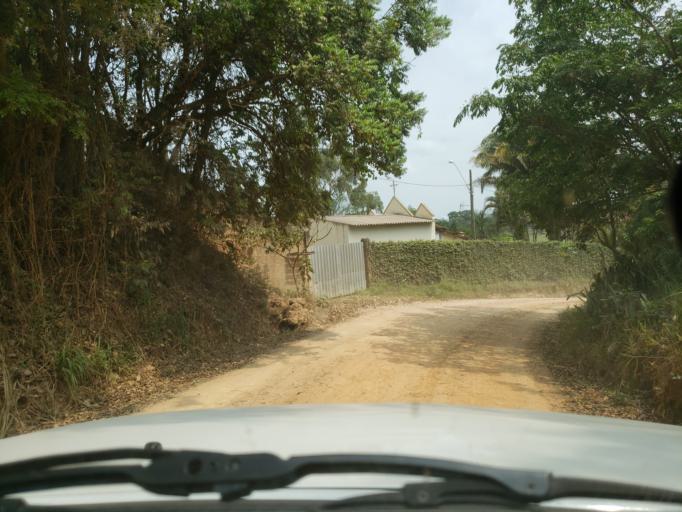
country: BR
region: Minas Gerais
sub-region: Jacutinga
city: Jacutinga
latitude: -22.3167
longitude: -46.6022
